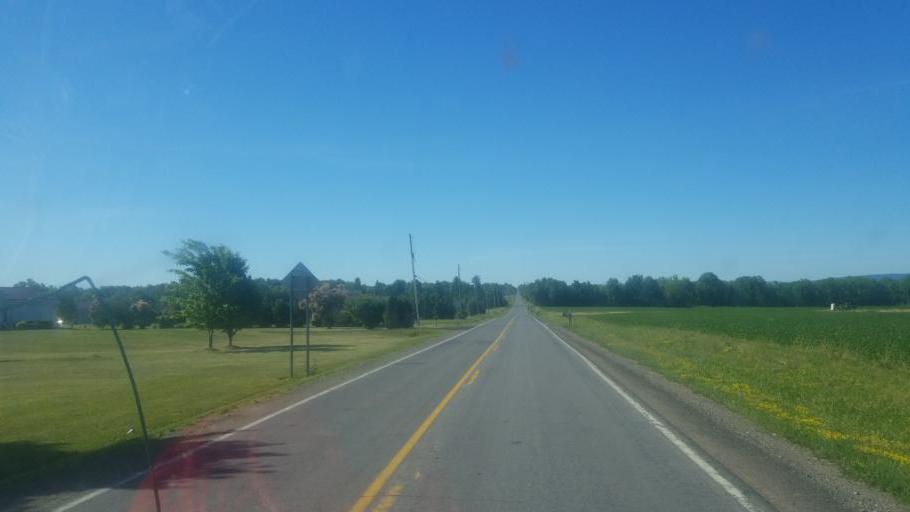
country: US
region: New York
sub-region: Ontario County
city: Canandaigua
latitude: 42.8428
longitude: -77.2305
